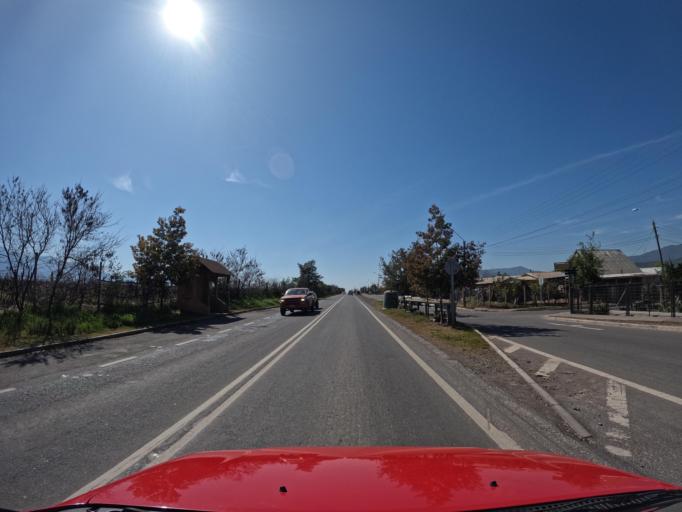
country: CL
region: Maule
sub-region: Provincia de Curico
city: Rauco
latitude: -35.0448
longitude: -71.4619
